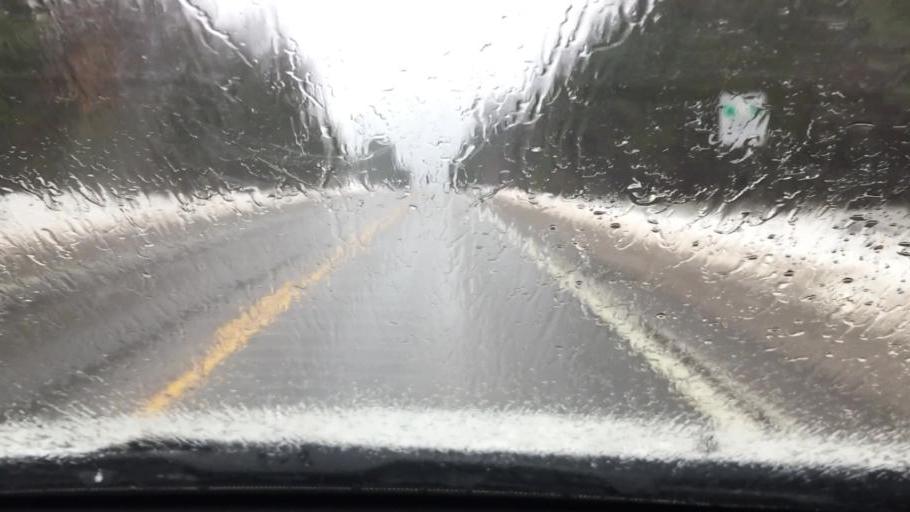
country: US
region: Michigan
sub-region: Charlevoix County
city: Charlevoix
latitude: 45.2646
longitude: -85.1992
